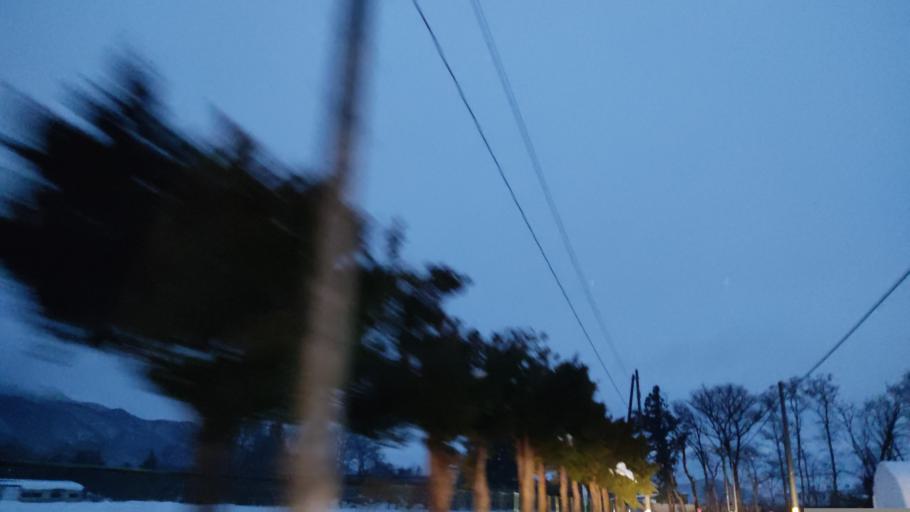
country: JP
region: Iwate
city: Morioka-shi
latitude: 39.6293
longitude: 141.1071
